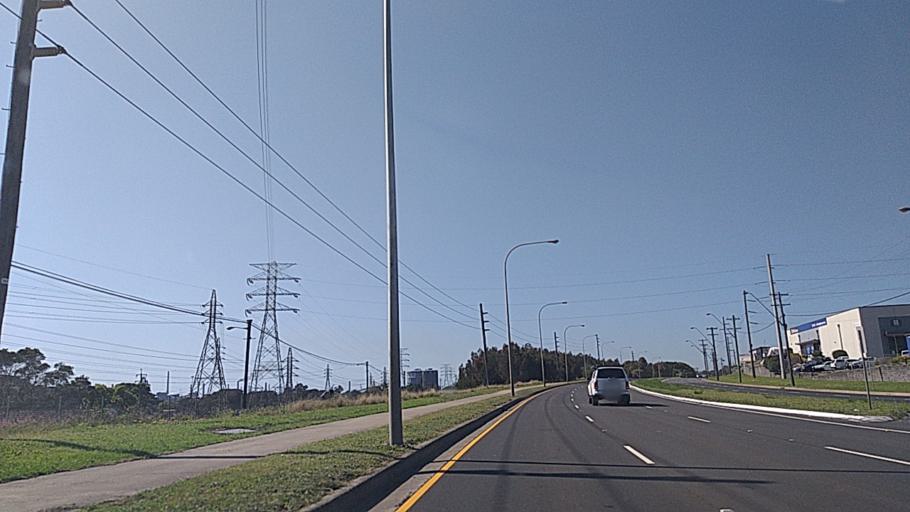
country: AU
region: New South Wales
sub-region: Wollongong
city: Mount Saint Thomas
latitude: -34.4593
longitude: 150.8654
